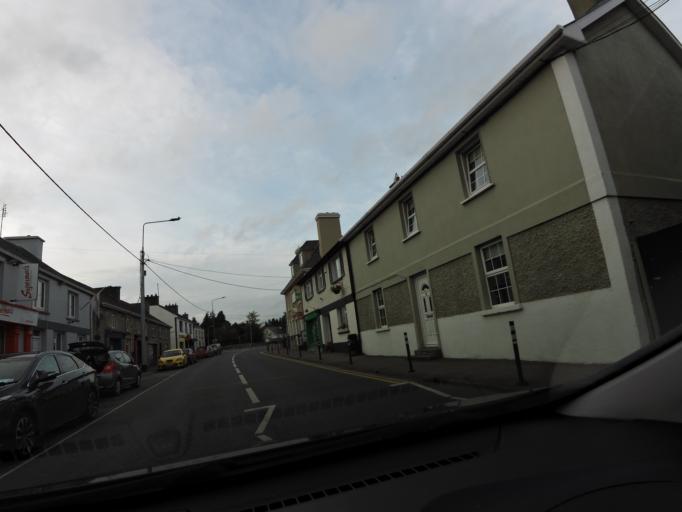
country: IE
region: Leinster
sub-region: Uibh Fhaili
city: Ferbane
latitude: 53.2722
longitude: -7.8280
